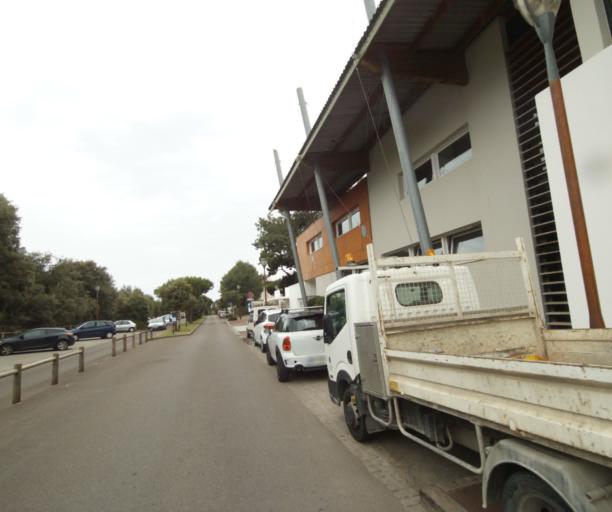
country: FR
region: Pays de la Loire
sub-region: Departement de la Vendee
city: Chateau-d'Olonne
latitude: 46.4853
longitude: -1.7570
